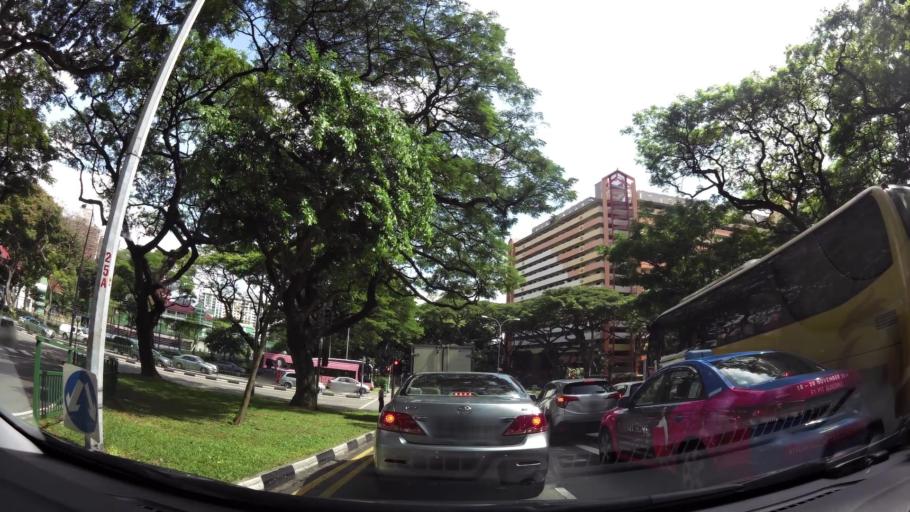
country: SG
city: Singapore
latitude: 1.2831
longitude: 103.8199
